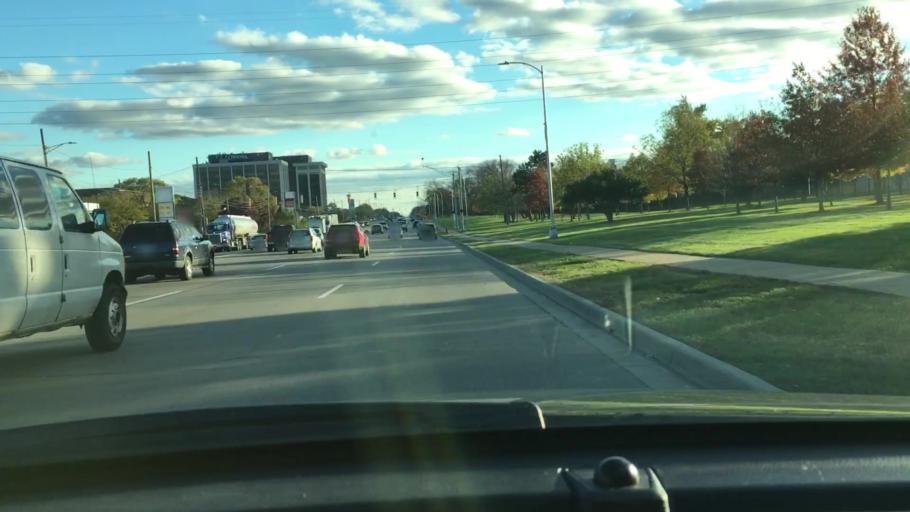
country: US
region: Michigan
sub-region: Macomb County
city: Center Line
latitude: 42.5223
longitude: -83.0290
